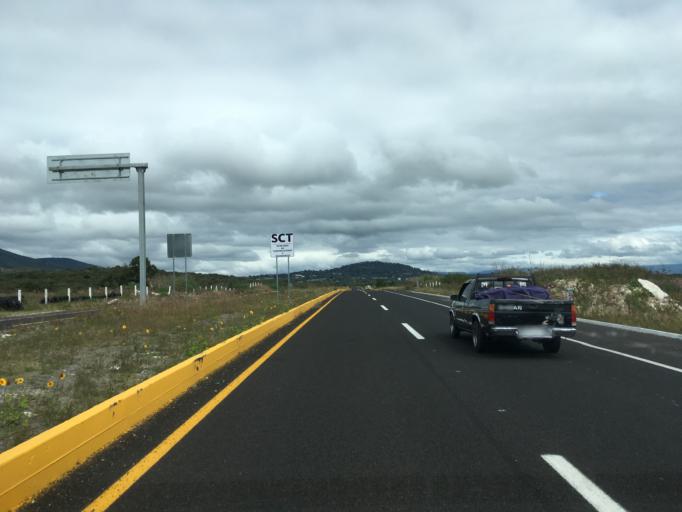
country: MX
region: Hidalgo
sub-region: Atotonilco el Grande
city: Santa Maria Amajac
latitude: 20.3703
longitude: -98.7205
